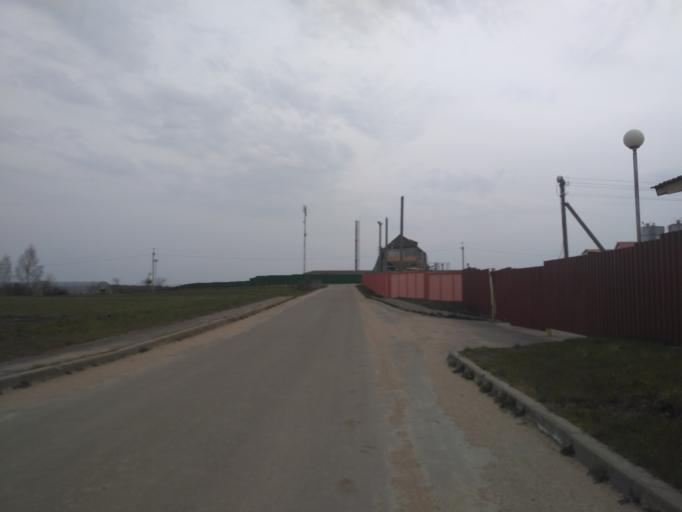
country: BY
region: Minsk
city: Slabada
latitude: 54.0042
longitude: 27.8797
